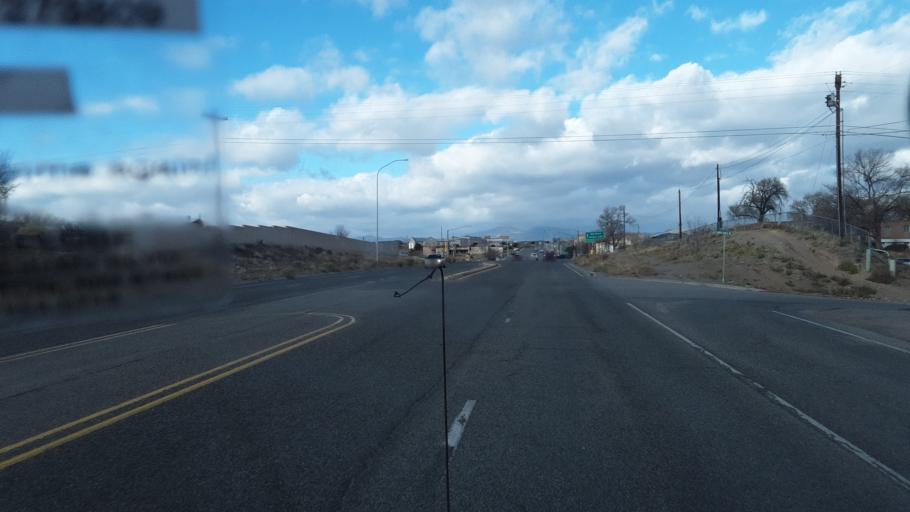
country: US
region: New Mexico
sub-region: Rio Arriba County
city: Espanola
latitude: 36.0083
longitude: -106.0853
